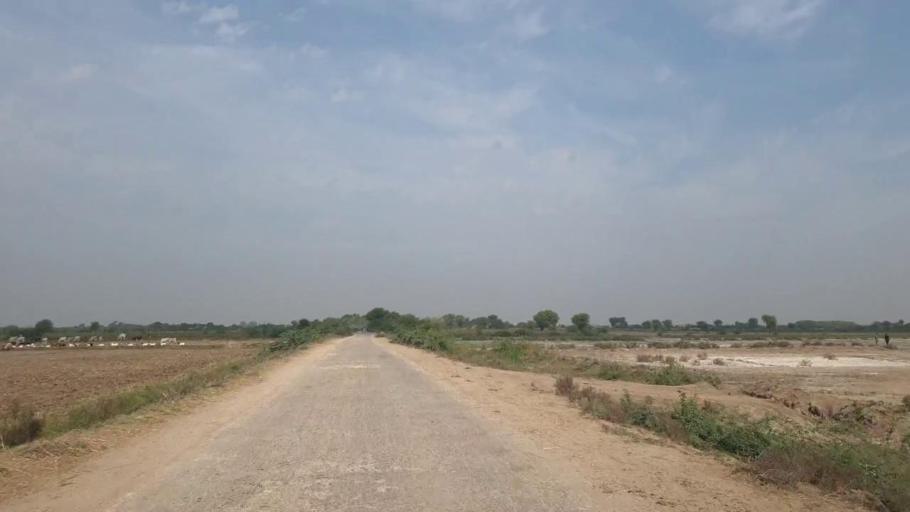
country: PK
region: Sindh
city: Rajo Khanani
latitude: 24.9329
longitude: 68.9878
